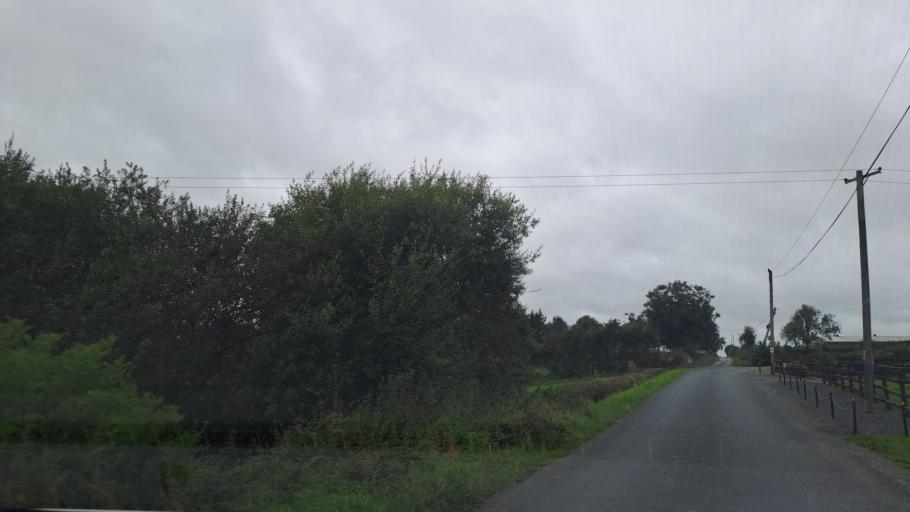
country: IE
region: Ulster
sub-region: An Cabhan
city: Kingscourt
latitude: 54.0018
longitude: -6.8520
